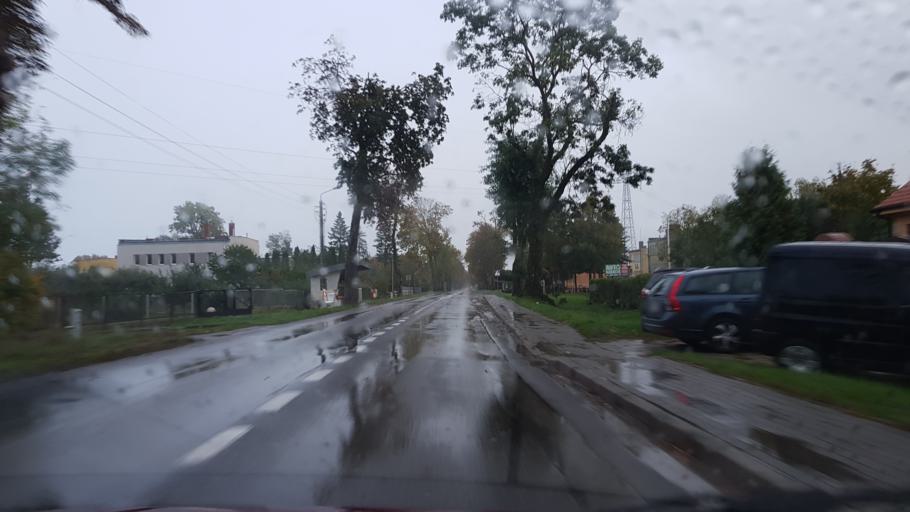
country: PL
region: Greater Poland Voivodeship
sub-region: Powiat pilski
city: Szydlowo
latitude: 53.1680
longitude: 16.5968
